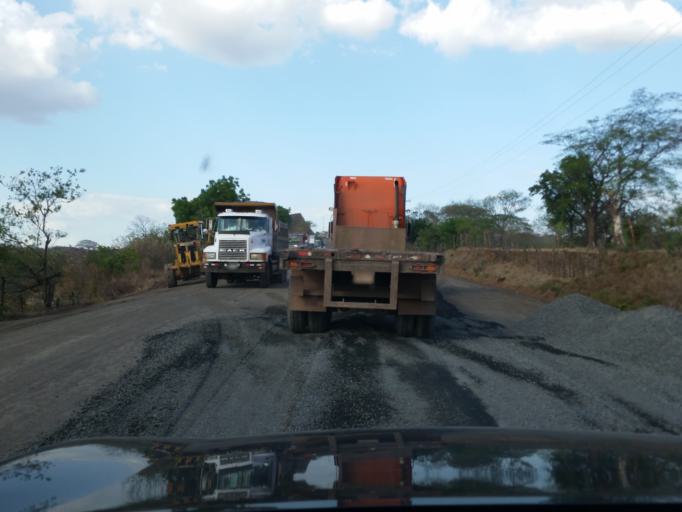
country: NI
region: Managua
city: Carlos Fonseca Amador
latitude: 12.0667
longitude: -86.4457
